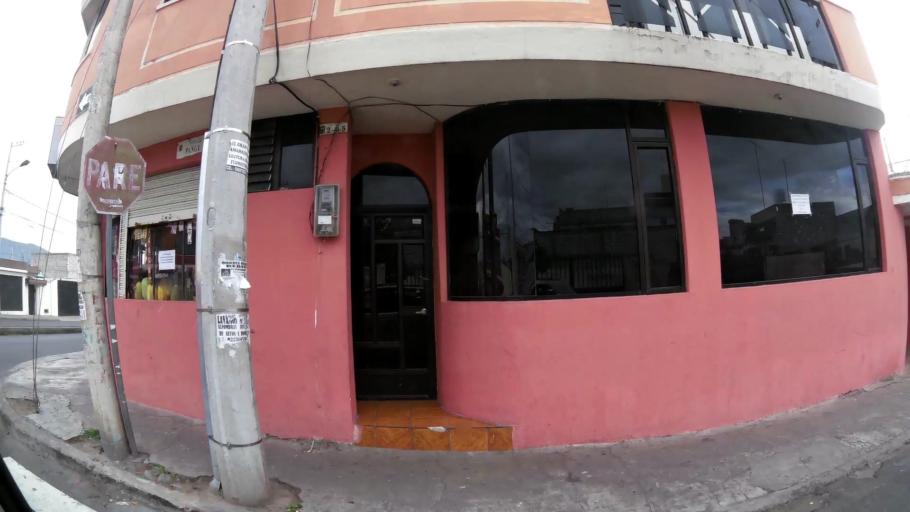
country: EC
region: Cotopaxi
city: Latacunga
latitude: -0.9297
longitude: -78.6265
